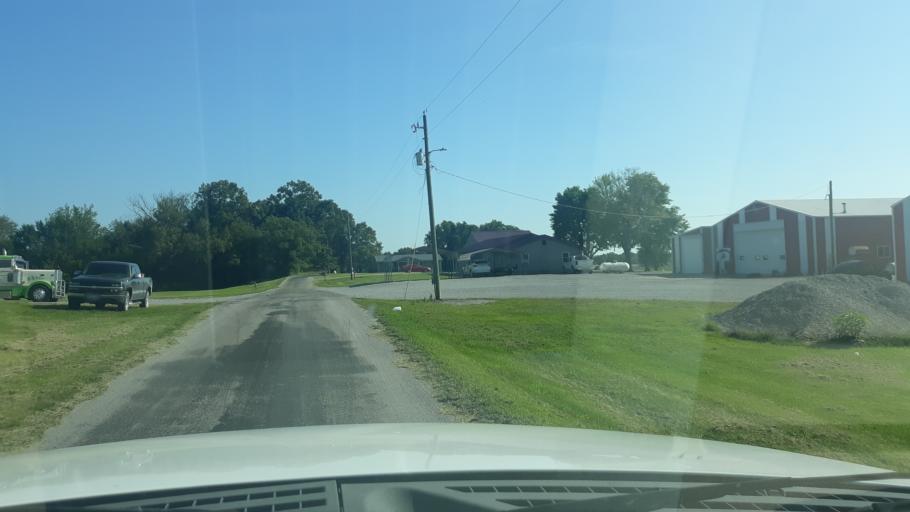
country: US
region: Illinois
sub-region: Saline County
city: Harrisburg
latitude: 37.8486
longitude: -88.6009
